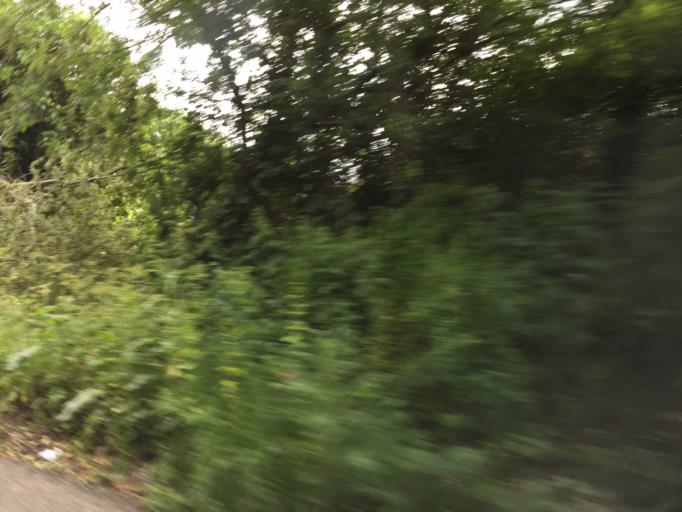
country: GB
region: England
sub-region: Wiltshire
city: Minety
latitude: 51.6510
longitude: -1.9383
